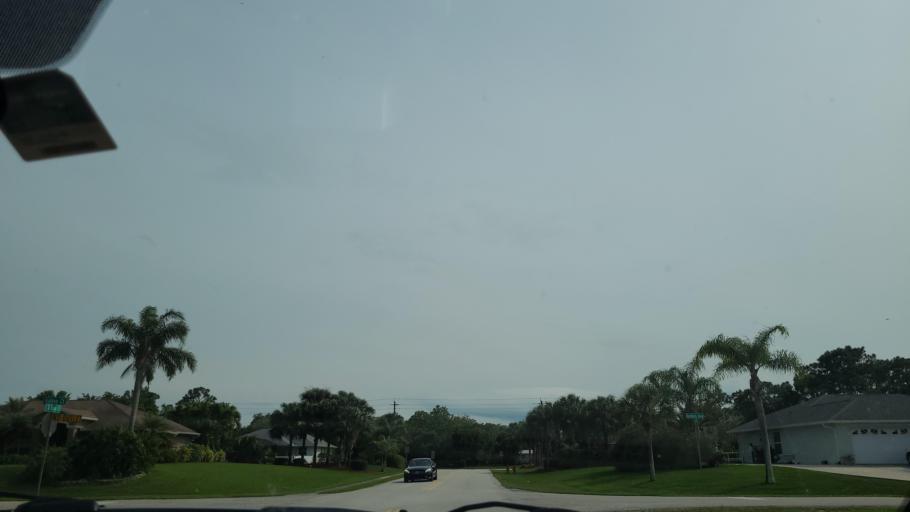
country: US
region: Florida
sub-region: Indian River County
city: Sebastian
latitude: 27.7793
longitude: -80.4758
